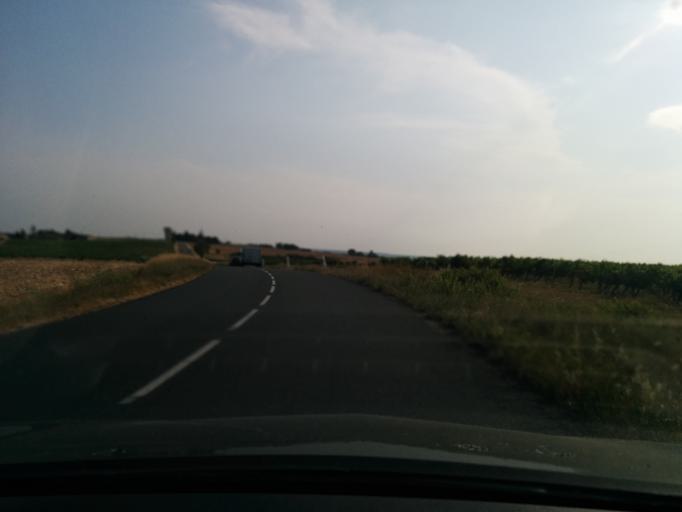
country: FR
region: Midi-Pyrenees
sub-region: Departement du Tarn
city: Cahuzac-sur-Vere
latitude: 44.0201
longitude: 1.9344
